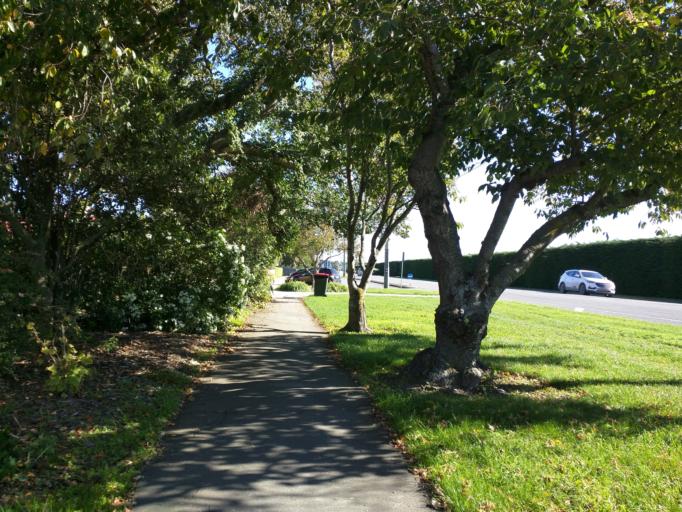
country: NZ
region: Canterbury
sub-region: Selwyn District
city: Lincoln
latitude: -43.6431
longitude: 172.4617
